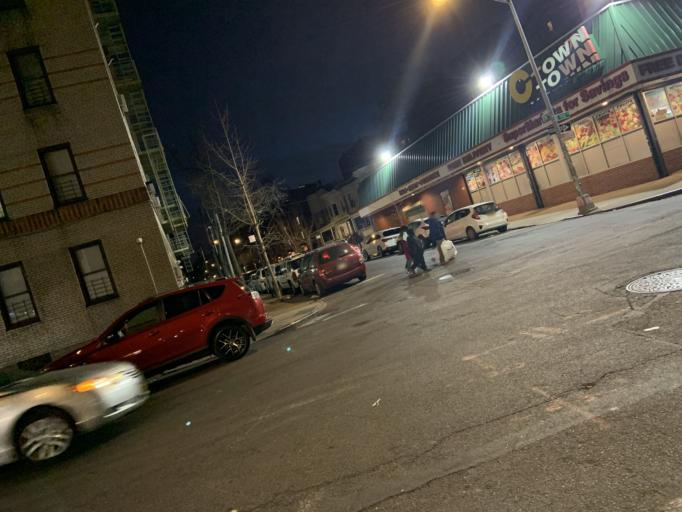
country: US
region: New York
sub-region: Bronx
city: The Bronx
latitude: 40.8707
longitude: -73.8919
